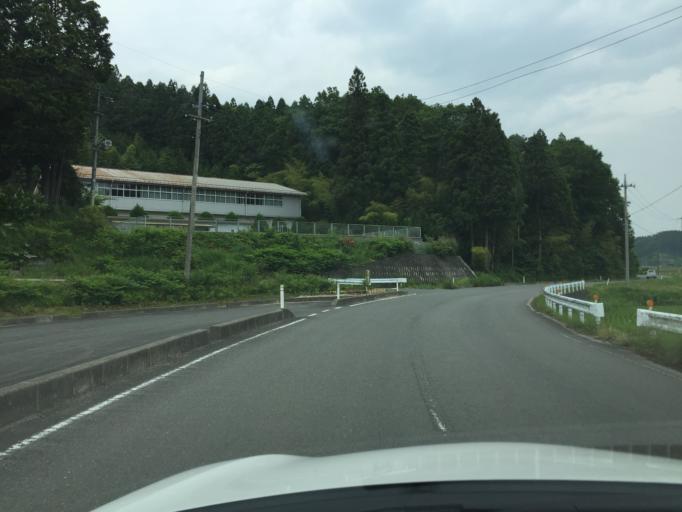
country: JP
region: Fukushima
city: Iwaki
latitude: 37.1835
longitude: 140.7175
